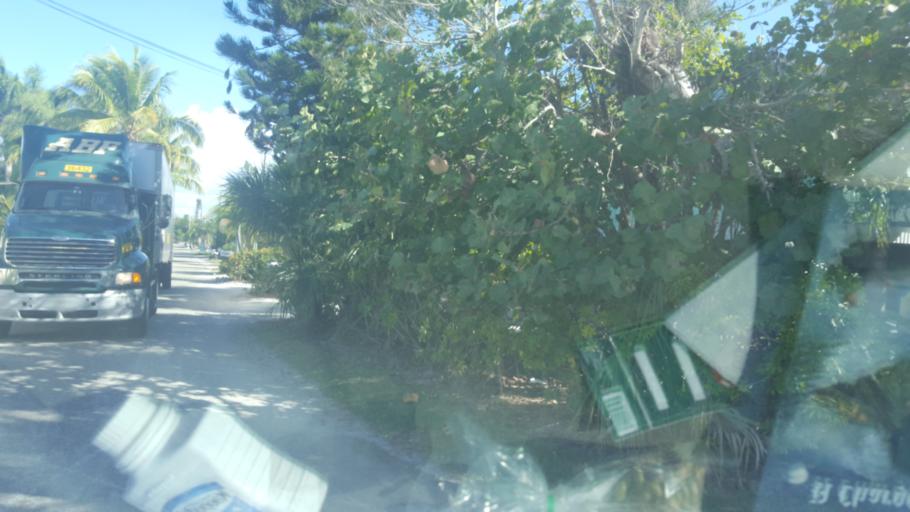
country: US
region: Florida
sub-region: Sarasota County
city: Gulf Gate Estates
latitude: 27.2471
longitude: -82.5341
